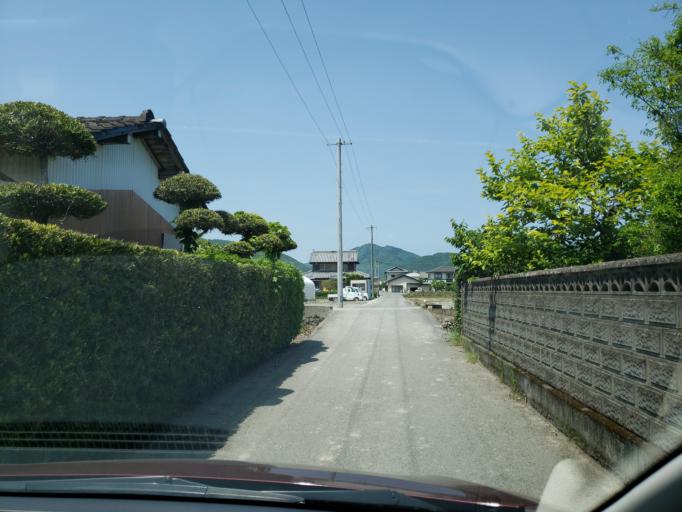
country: JP
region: Tokushima
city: Kamojimacho-jogejima
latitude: 34.0894
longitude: 134.2681
